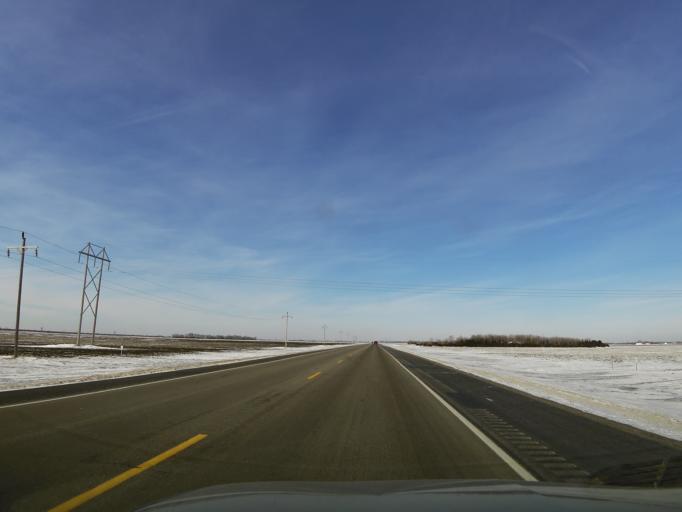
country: US
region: North Dakota
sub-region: Walsh County
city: Grafton
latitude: 48.4122
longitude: -97.2656
